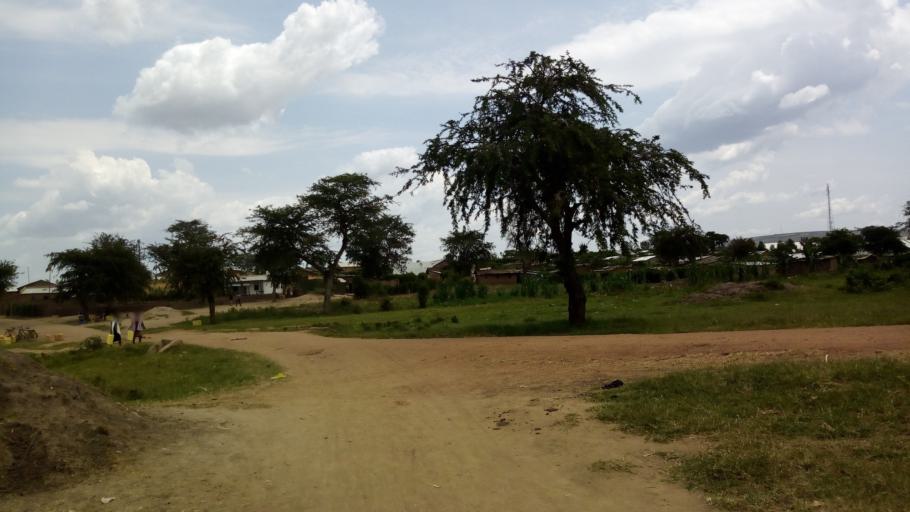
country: UG
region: Western Region
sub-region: Isingiro District
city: Isingiro
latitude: -0.7726
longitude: 30.9460
